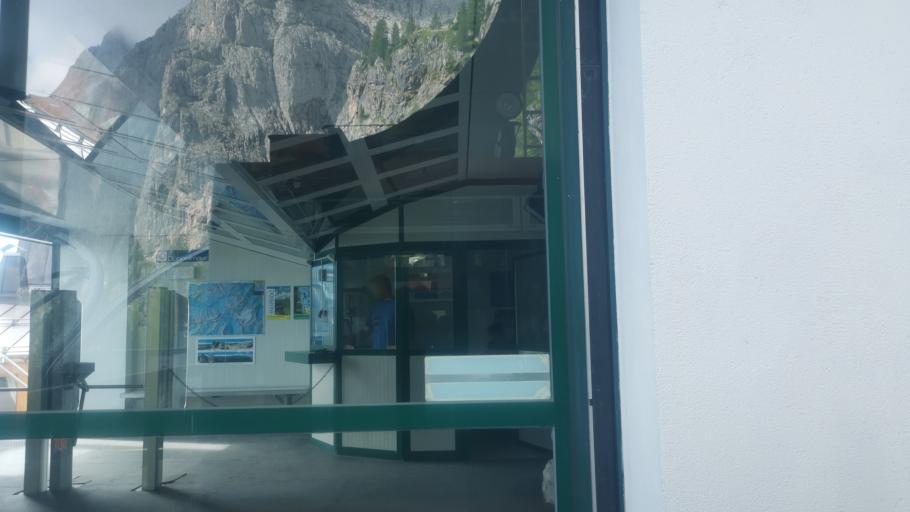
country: IT
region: Trentino-Alto Adige
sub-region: Provincia di Trento
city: Siror
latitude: 46.2721
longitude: 11.8213
